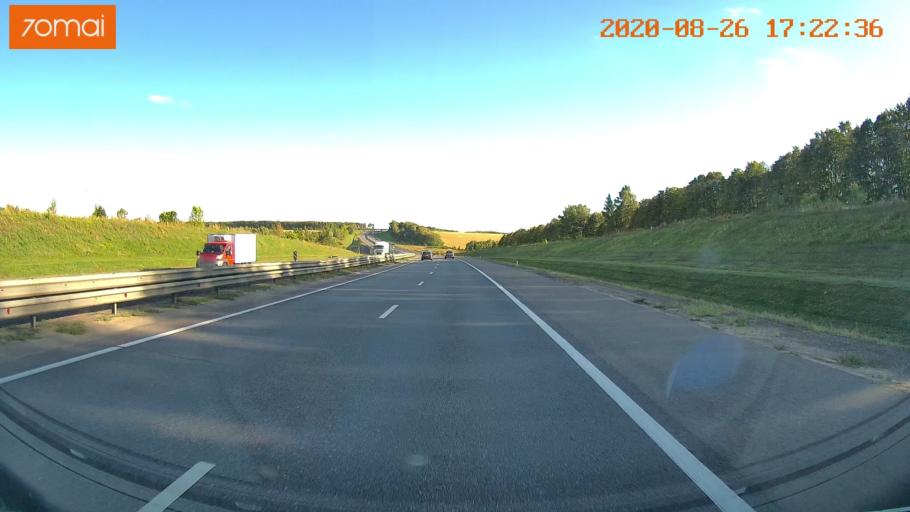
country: RU
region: Tula
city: Volovo
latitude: 53.5475
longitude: 38.1130
